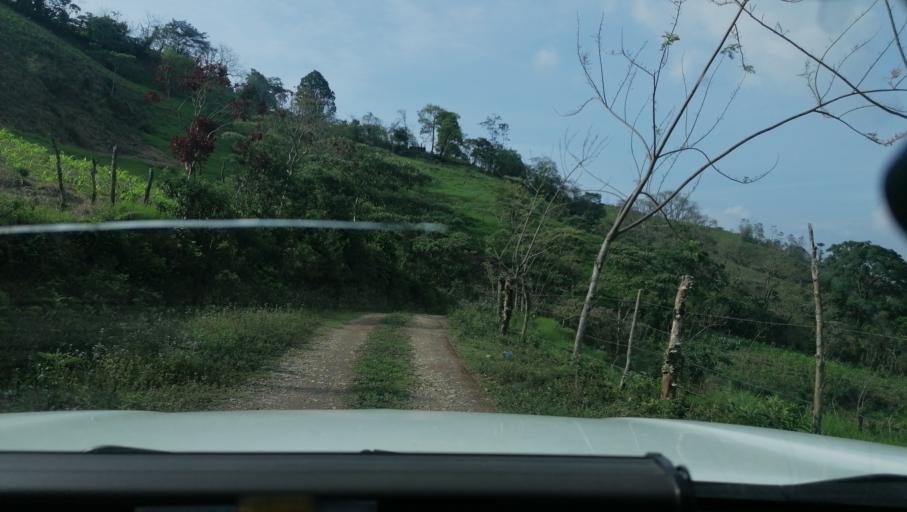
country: MX
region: Chiapas
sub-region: Tapilula
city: San Francisco Jacona
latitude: 17.3039
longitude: -93.1031
